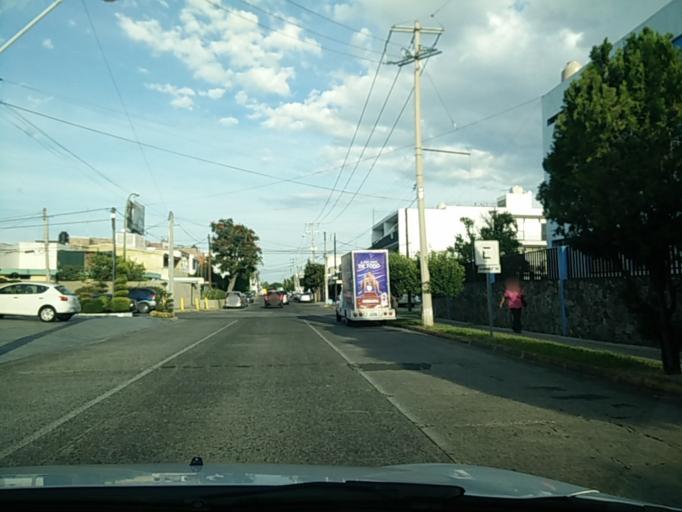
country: MX
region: Jalisco
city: Guadalajara
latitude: 20.6899
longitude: -103.3752
